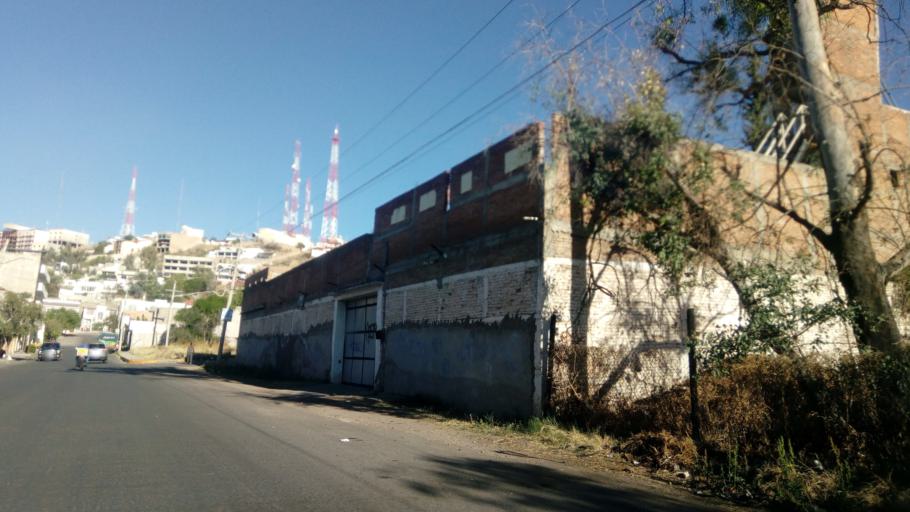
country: MX
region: Durango
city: Victoria de Durango
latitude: 24.0221
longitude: -104.6887
